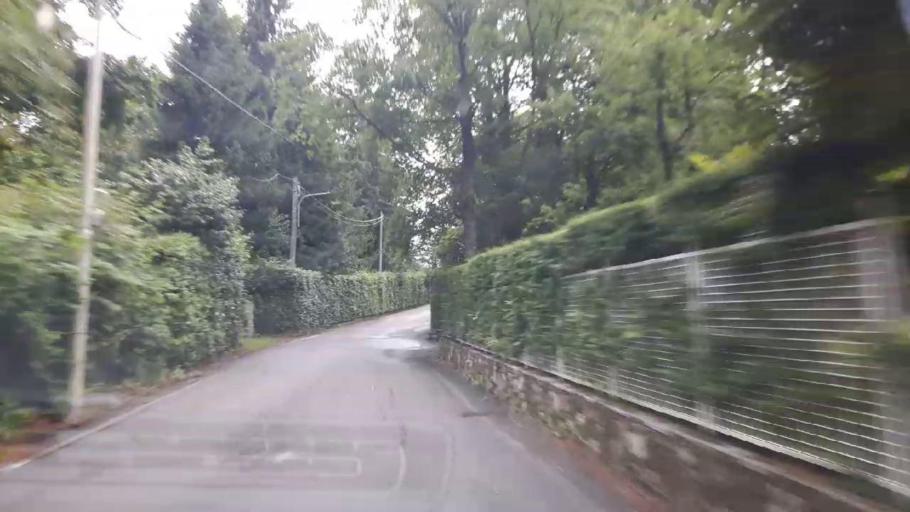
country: IT
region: Piedmont
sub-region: Provincia Verbano-Cusio-Ossola
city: Gignese
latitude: 45.8659
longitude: 8.5095
